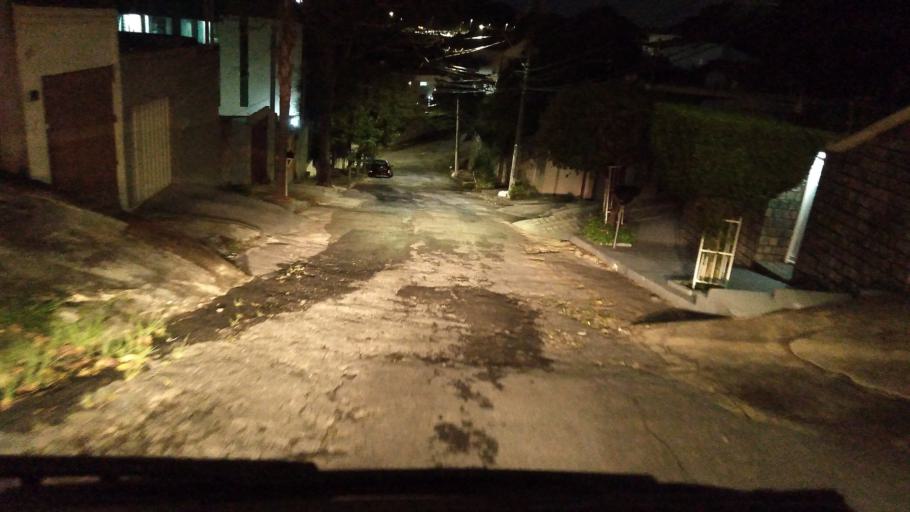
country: BR
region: Minas Gerais
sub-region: Belo Horizonte
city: Belo Horizonte
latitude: -19.8972
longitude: -43.9741
